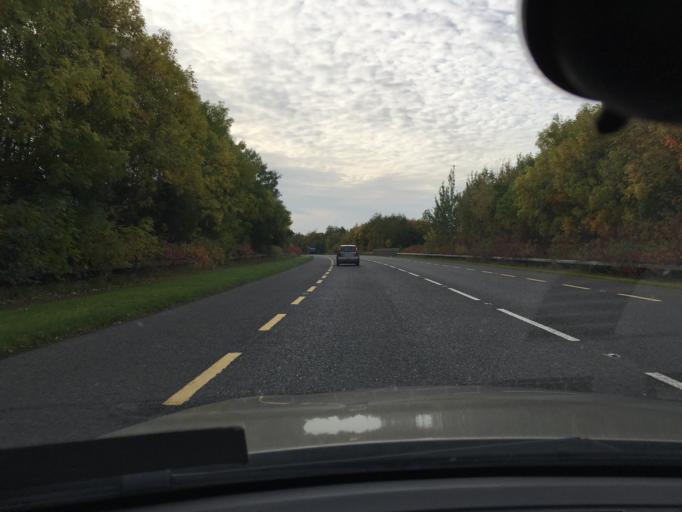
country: IE
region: Leinster
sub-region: An Longfort
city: Longford
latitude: 53.7416
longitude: -7.7861
